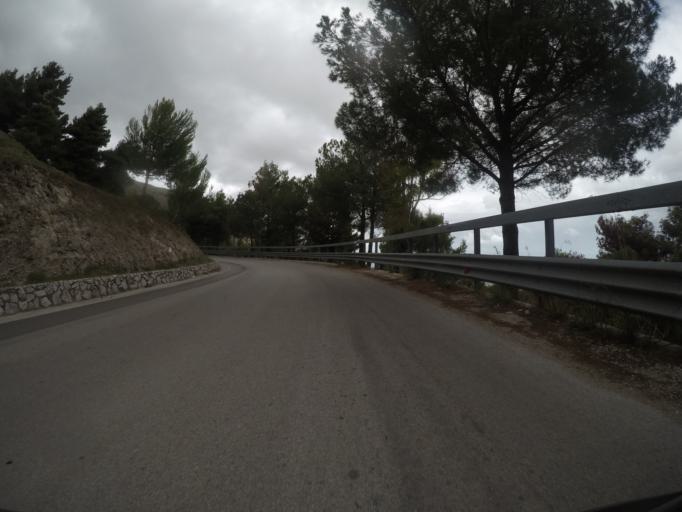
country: IT
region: Sicily
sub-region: Palermo
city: Montelepre
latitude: 38.1155
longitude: 13.1703
